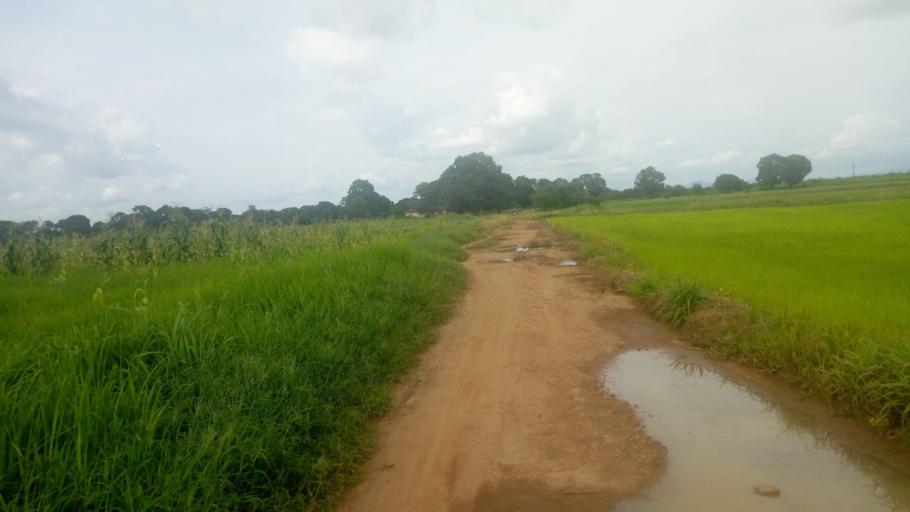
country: SL
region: Northern Province
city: Magburaka
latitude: 8.6749
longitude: -12.0145
